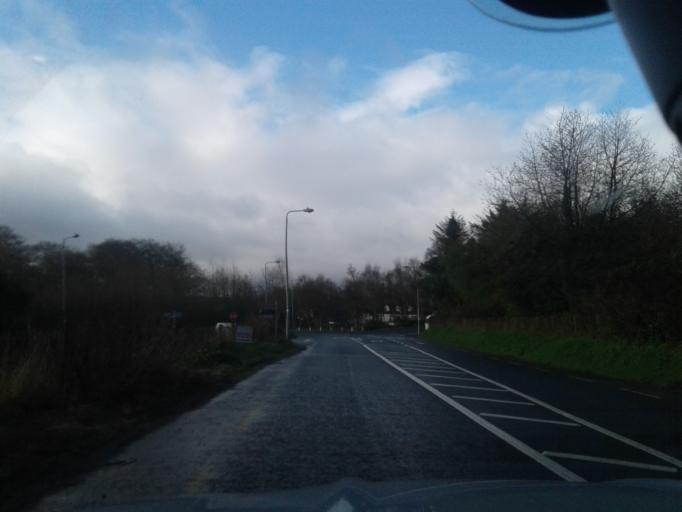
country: IE
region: Ulster
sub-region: County Donegal
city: Letterkenny
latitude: 54.9659
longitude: -7.6910
